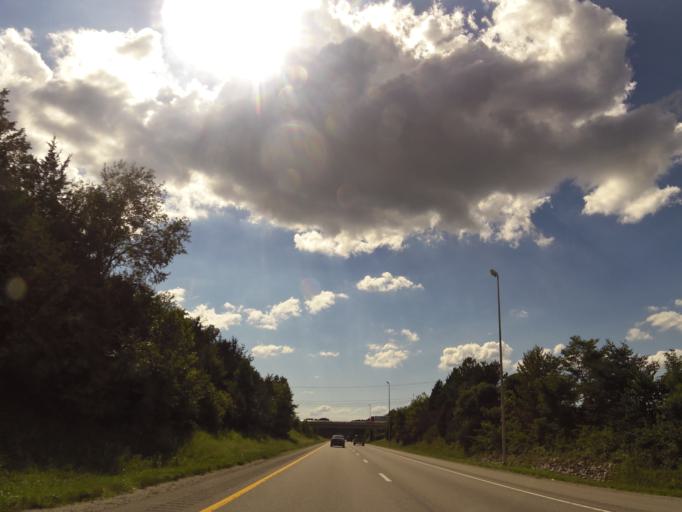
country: US
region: Tennessee
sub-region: Putnam County
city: Cookeville
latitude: 36.1368
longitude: -85.5266
